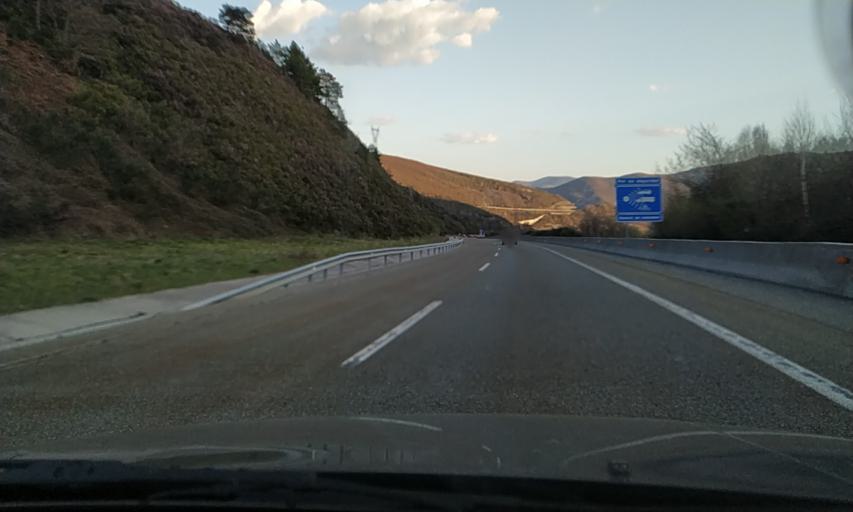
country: ES
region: Castille and Leon
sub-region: Provincia de Leon
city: Vega de Valcarce
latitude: 42.6967
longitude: -6.9968
